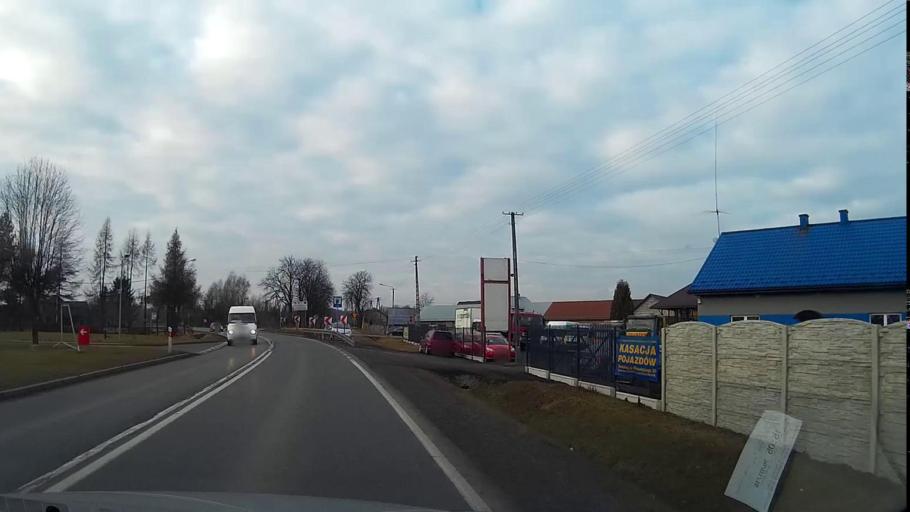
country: PL
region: Lesser Poland Voivodeship
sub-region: Powiat chrzanowski
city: Alwernia
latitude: 50.0606
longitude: 19.5544
